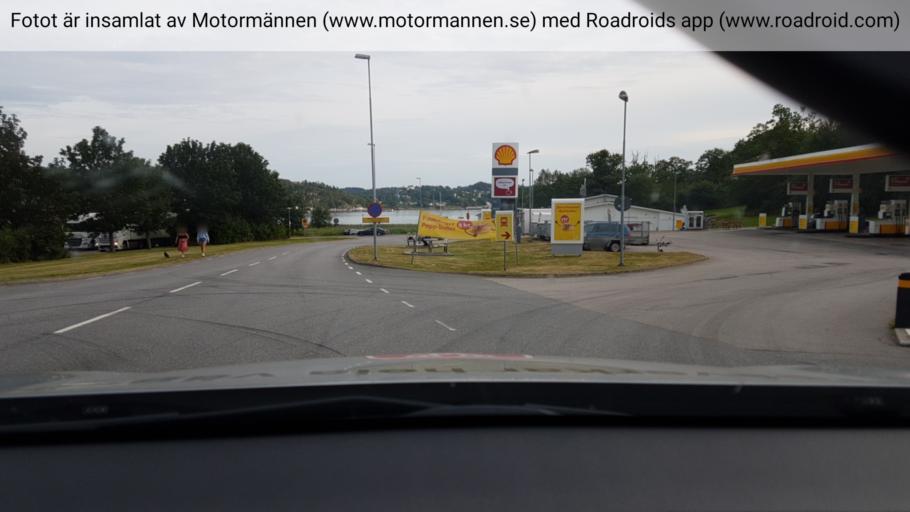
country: SE
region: Vaestra Goetaland
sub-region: Uddevalla Kommun
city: Ljungskile
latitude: 58.2308
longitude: 11.9101
